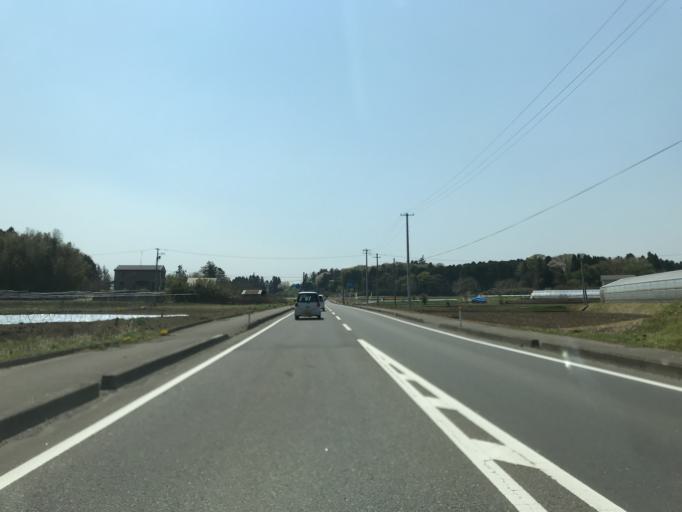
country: JP
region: Fukushima
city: Ishikawa
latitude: 37.1739
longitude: 140.3493
